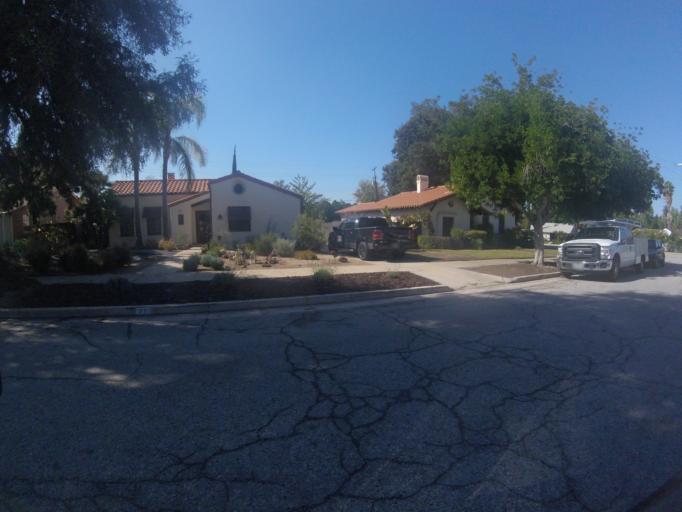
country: US
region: California
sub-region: San Bernardino County
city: Redlands
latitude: 34.0563
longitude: -117.1912
